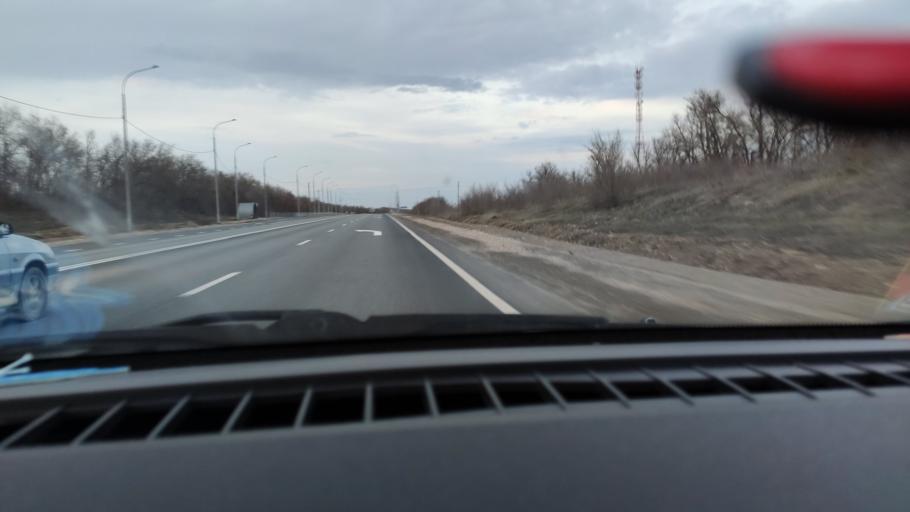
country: RU
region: Saratov
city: Yelshanka
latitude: 51.8952
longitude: 46.5300
